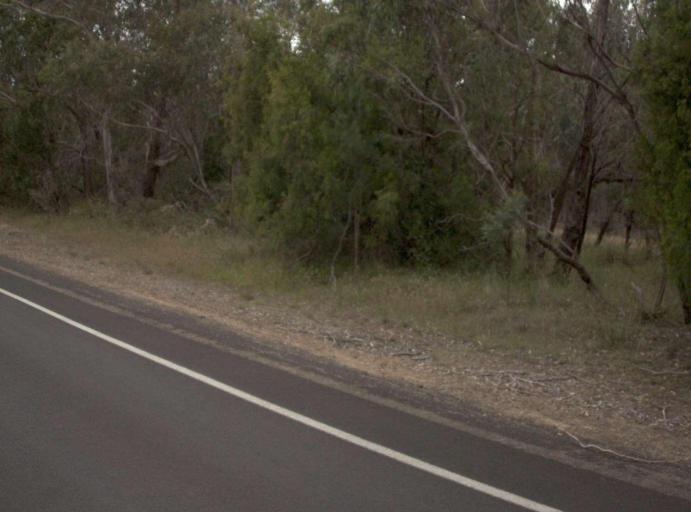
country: AU
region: Victoria
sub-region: Wellington
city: Sale
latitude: -38.4246
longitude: 146.9556
